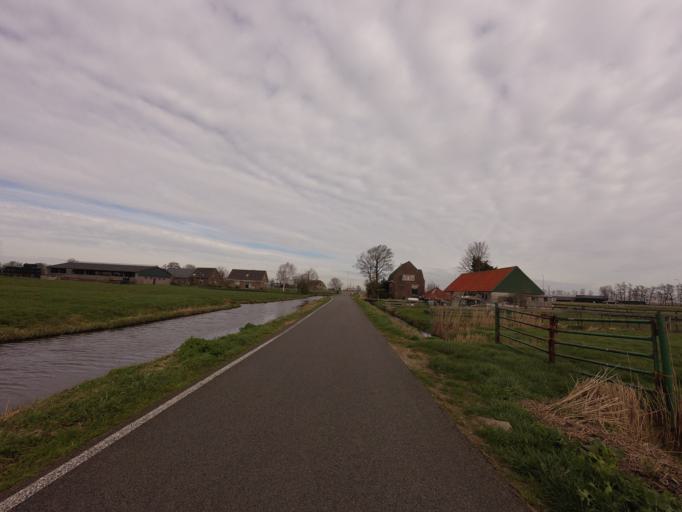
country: NL
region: Utrecht
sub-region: Gemeente De Ronde Venen
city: Mijdrecht
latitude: 52.2215
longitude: 4.8615
